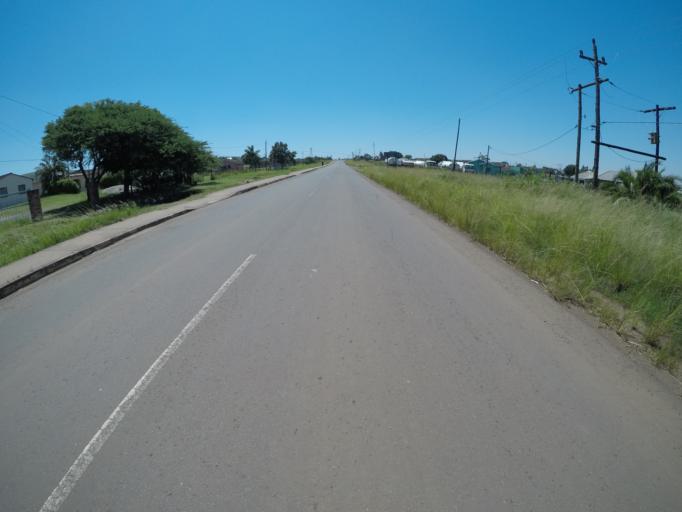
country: ZA
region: KwaZulu-Natal
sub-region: uThungulu District Municipality
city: Empangeni
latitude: -28.7129
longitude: 31.8664
